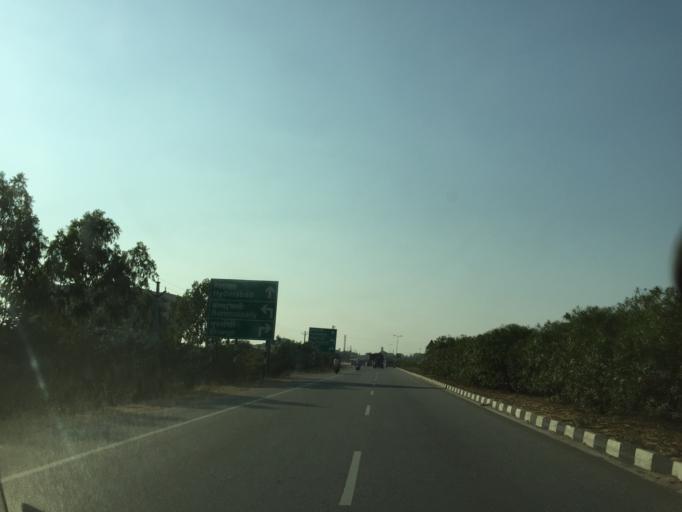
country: IN
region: Telangana
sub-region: Nalgonda
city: Bhongir
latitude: 17.5027
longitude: 78.8762
